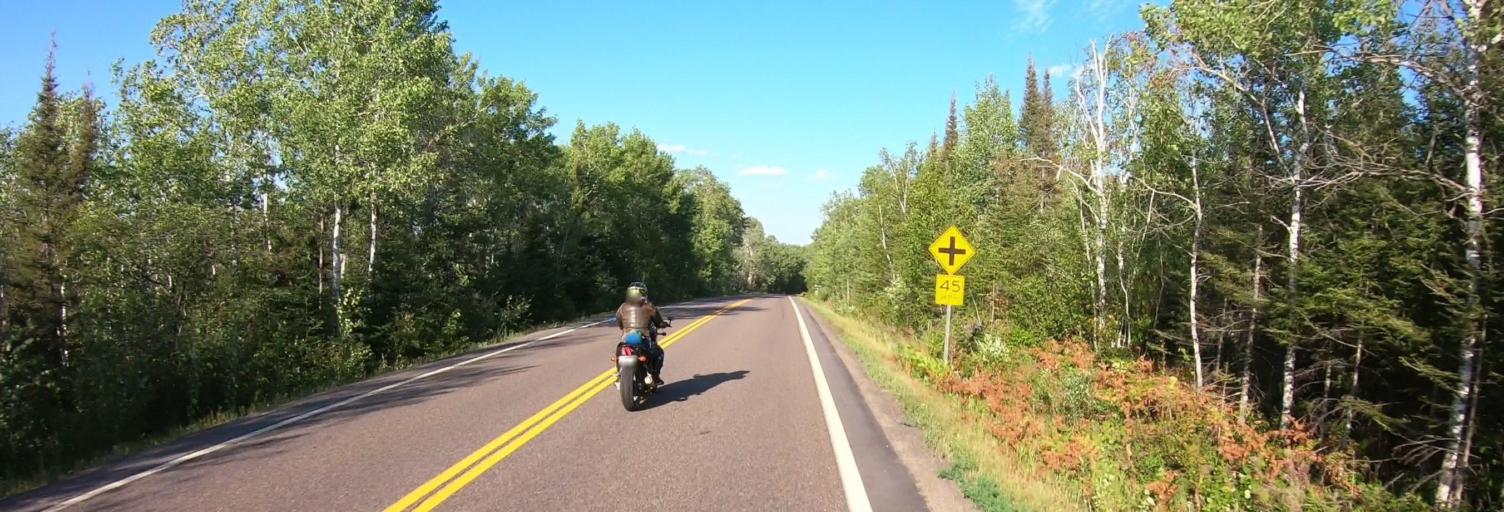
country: US
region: Minnesota
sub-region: Saint Louis County
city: Ely
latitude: 47.9610
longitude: -91.5694
